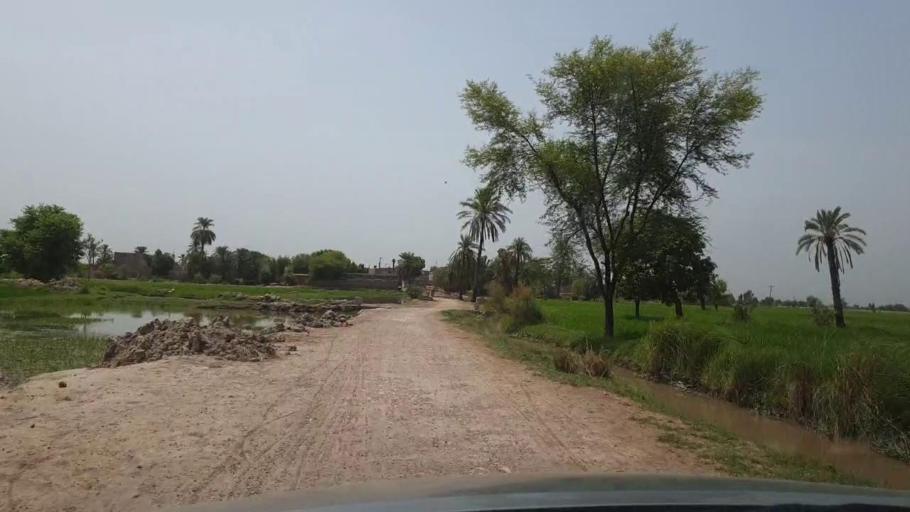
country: PK
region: Sindh
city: Madeji
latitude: 27.7885
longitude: 68.4342
